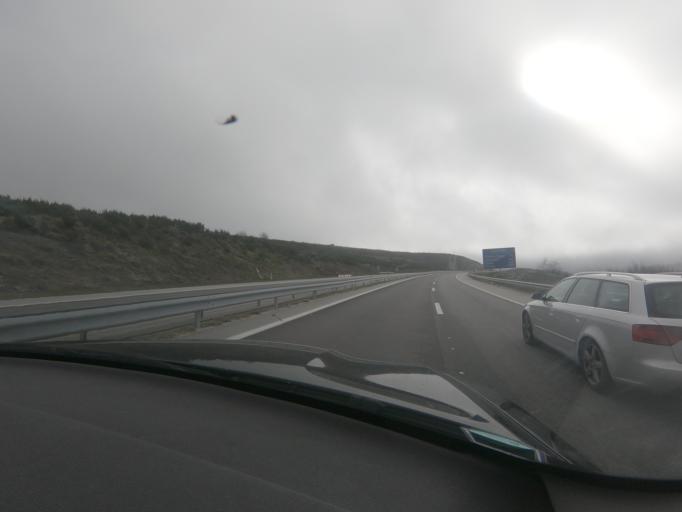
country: PT
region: Viseu
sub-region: Tarouca
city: Tarouca
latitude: 40.9950
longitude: -7.8818
